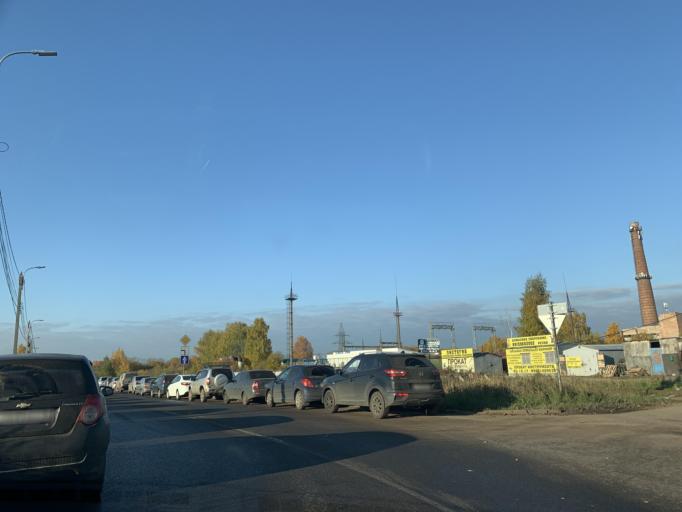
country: RU
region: Jaroslavl
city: Yaroslavl
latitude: 57.6810
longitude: 39.7622
